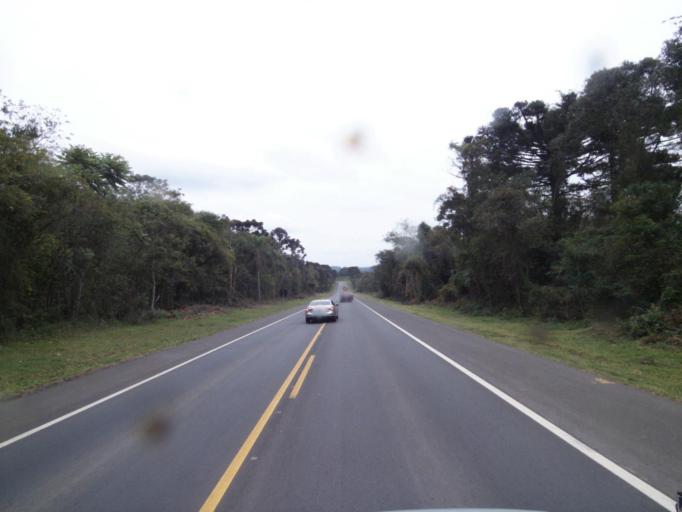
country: BR
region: Parana
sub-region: Irati
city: Irati
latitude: -25.4642
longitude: -50.5436
